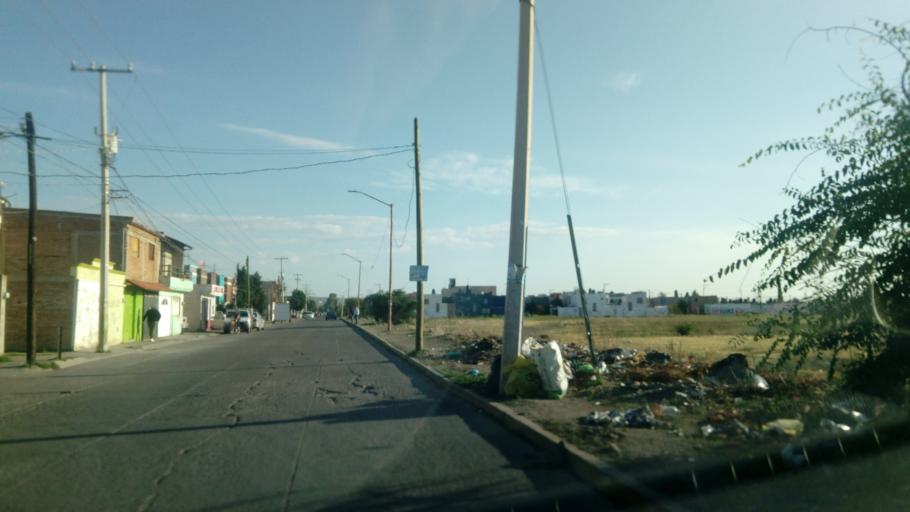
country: MX
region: Durango
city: Victoria de Durango
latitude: 24.0666
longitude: -104.5862
